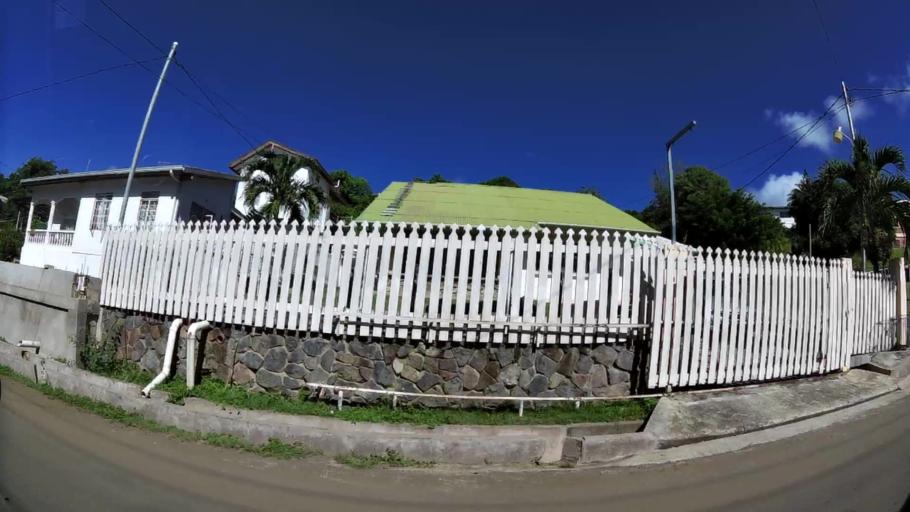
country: TT
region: Tobago
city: Scarborough
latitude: 11.1731
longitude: -60.7235
